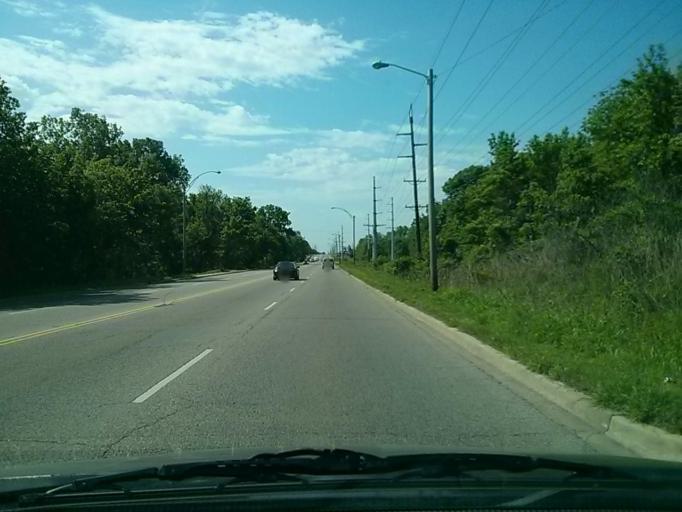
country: US
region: Oklahoma
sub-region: Tulsa County
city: Turley
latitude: 36.2159
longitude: -95.9757
